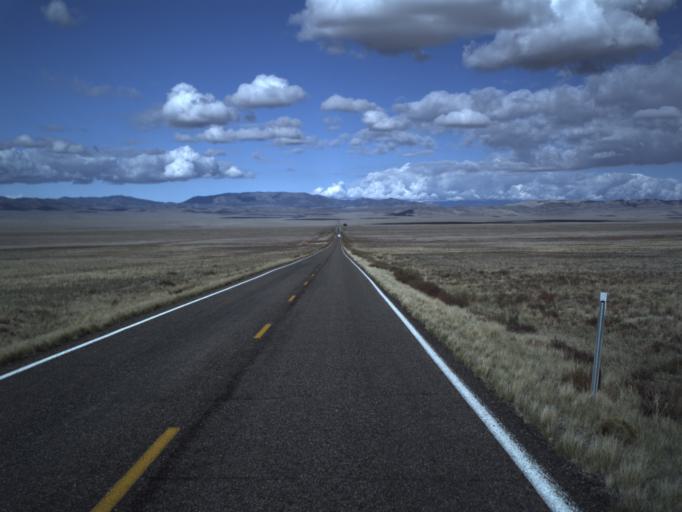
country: US
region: Utah
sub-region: Beaver County
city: Milford
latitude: 38.5172
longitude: -113.6410
